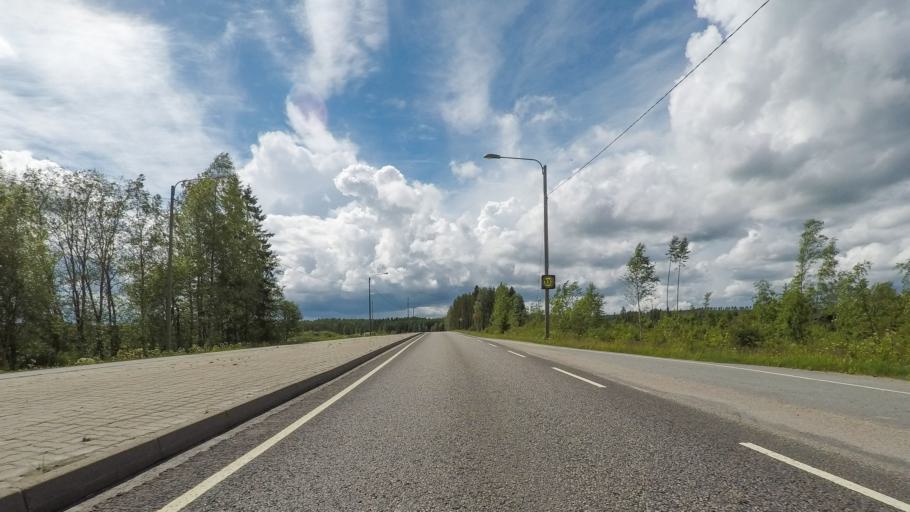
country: FI
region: Central Finland
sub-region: Jyvaeskylae
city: Hankasalmi
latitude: 62.2995
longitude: 26.4566
